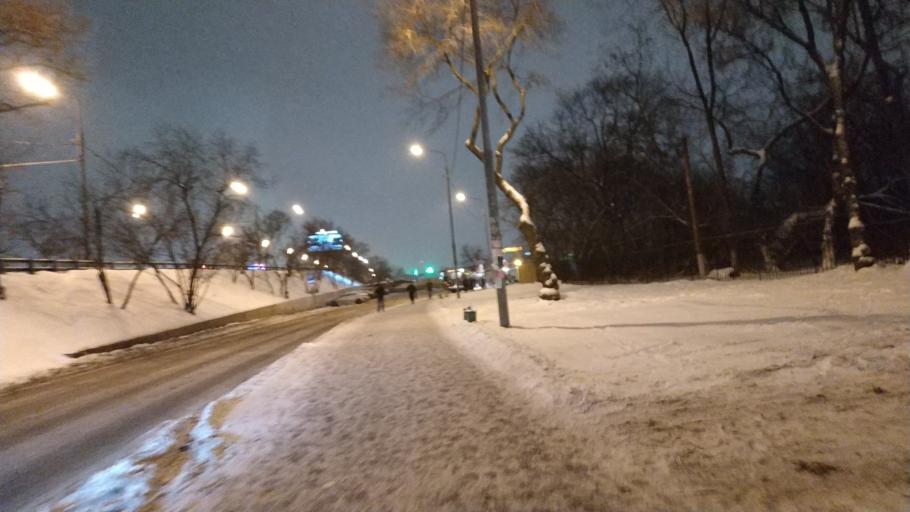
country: RU
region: Moscow
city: Taganskiy
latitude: 55.7263
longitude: 37.6836
